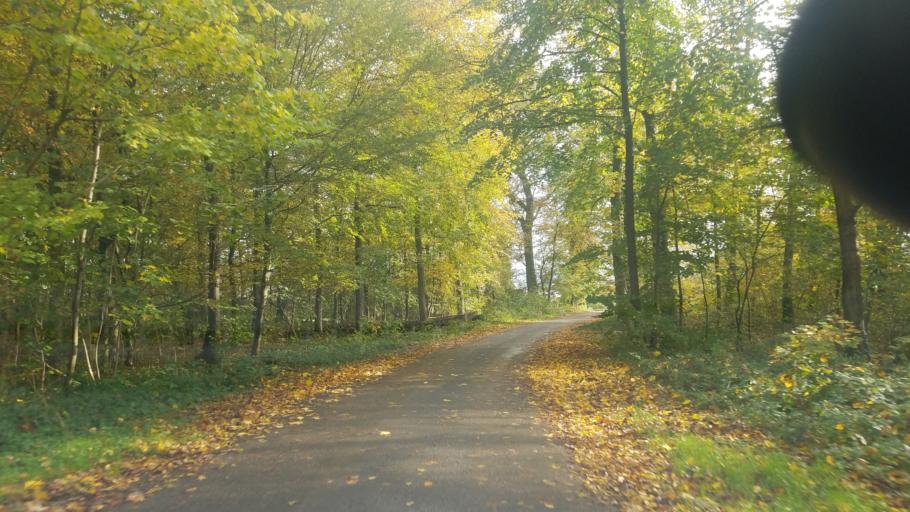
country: DE
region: Baden-Wuerttemberg
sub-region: Freiburg Region
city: Rheinau
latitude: 48.6759
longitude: 7.9801
